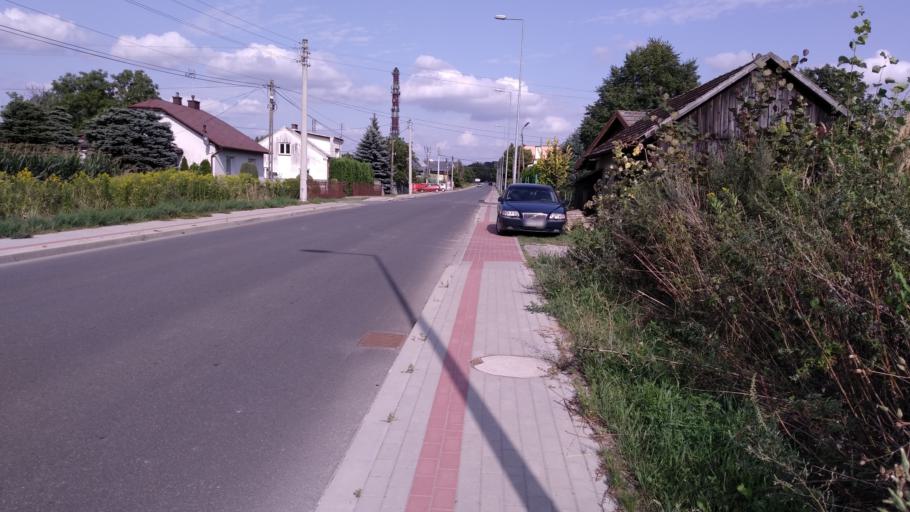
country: PL
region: Subcarpathian Voivodeship
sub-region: Powiat lancucki
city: Lancut
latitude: 50.0788
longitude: 22.2181
